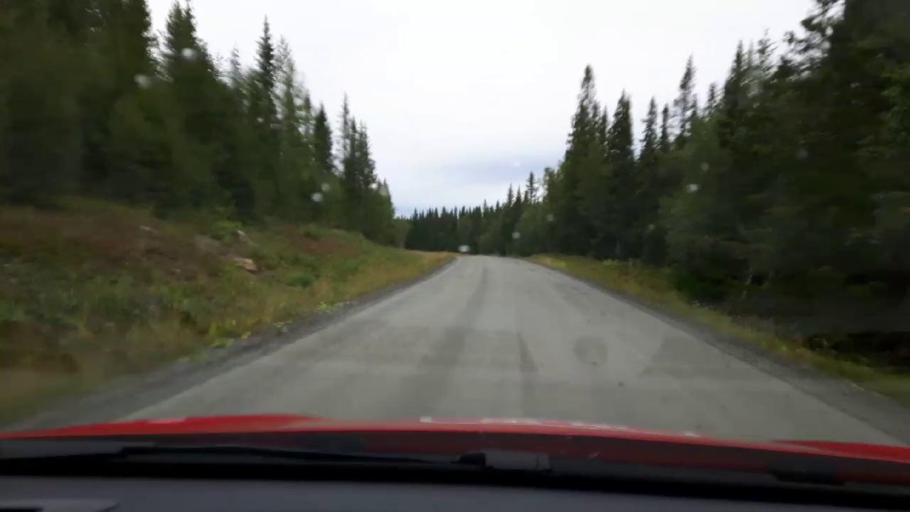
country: SE
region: Jaemtland
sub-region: Are Kommun
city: Are
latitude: 63.4338
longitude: 13.2726
